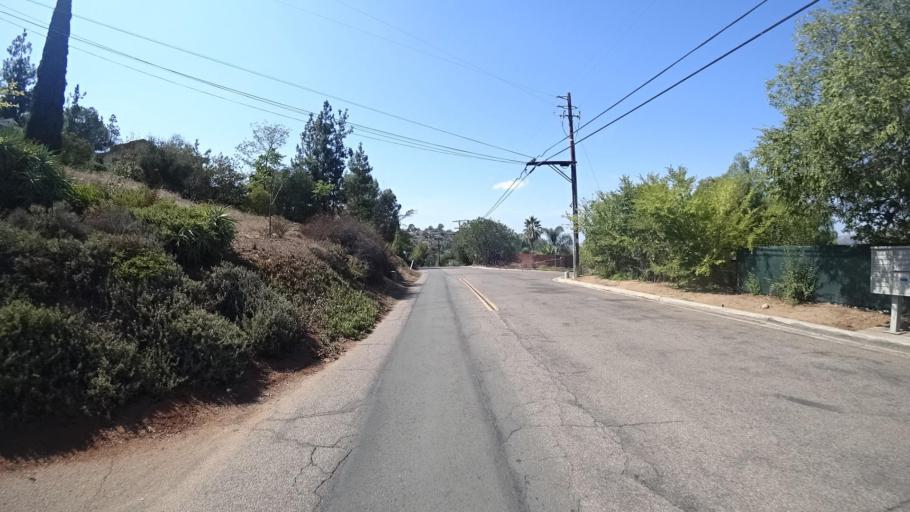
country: US
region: California
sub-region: San Diego County
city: Bostonia
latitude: 32.7790
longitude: -116.9244
